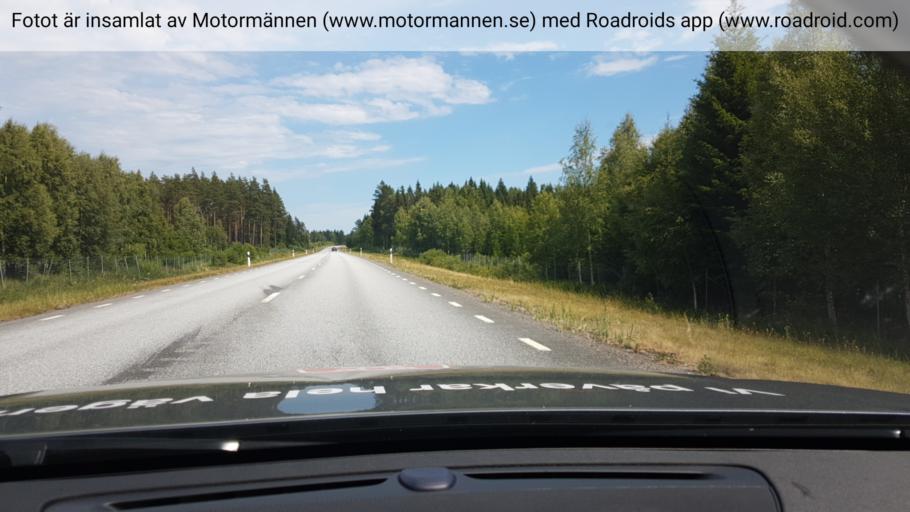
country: SE
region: Uppsala
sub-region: Osthammars Kommun
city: OEsthammar
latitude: 60.1727
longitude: 18.3352
